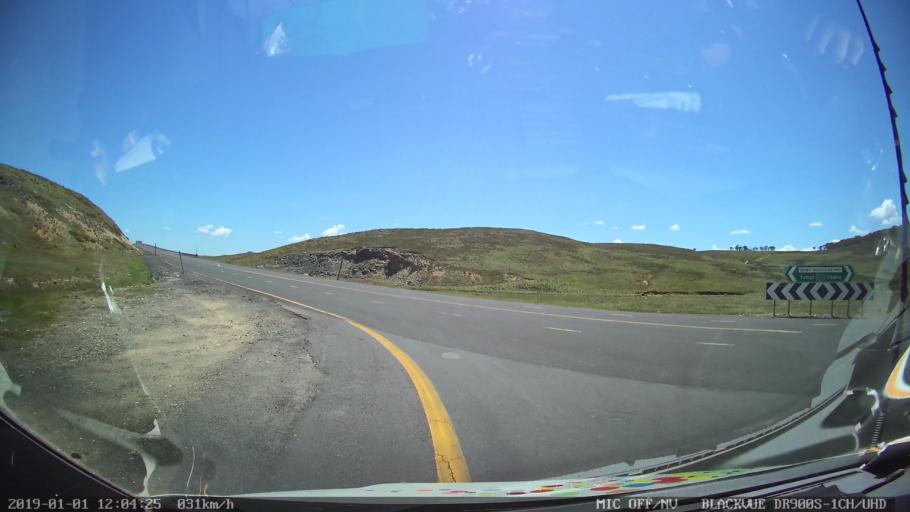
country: AU
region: New South Wales
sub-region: Snowy River
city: Jindabyne
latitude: -35.8668
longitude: 148.4973
